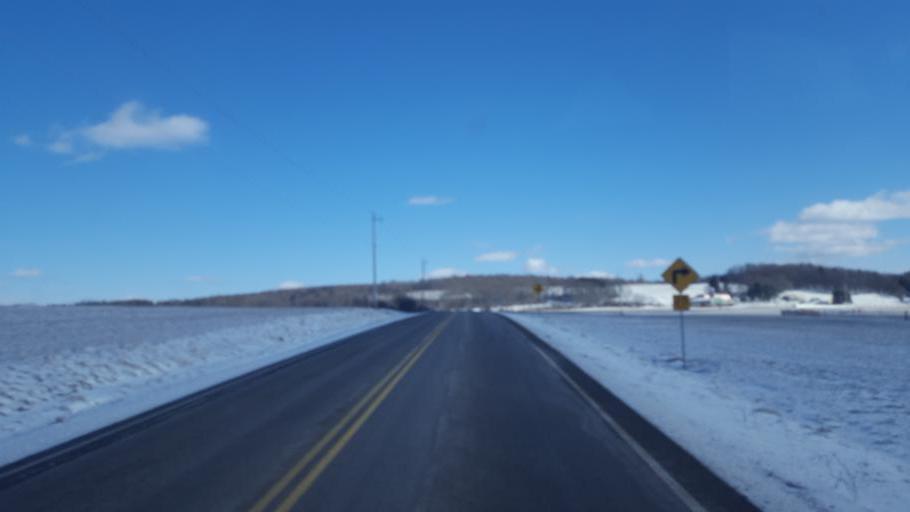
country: US
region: New York
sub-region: Allegany County
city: Friendship
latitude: 42.1941
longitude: -78.0949
